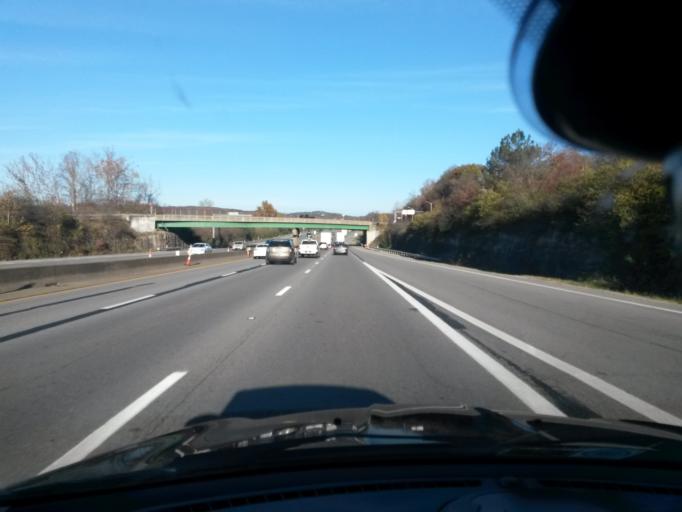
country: US
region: West Virginia
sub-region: Kanawha County
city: South Charleston
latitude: 38.3597
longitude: -81.6988
